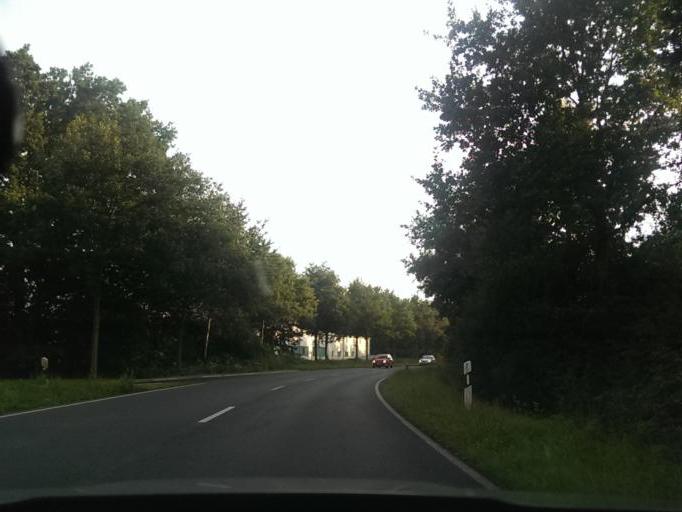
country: DE
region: Lower Saxony
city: Lilienthal
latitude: 53.1453
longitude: 8.9022
